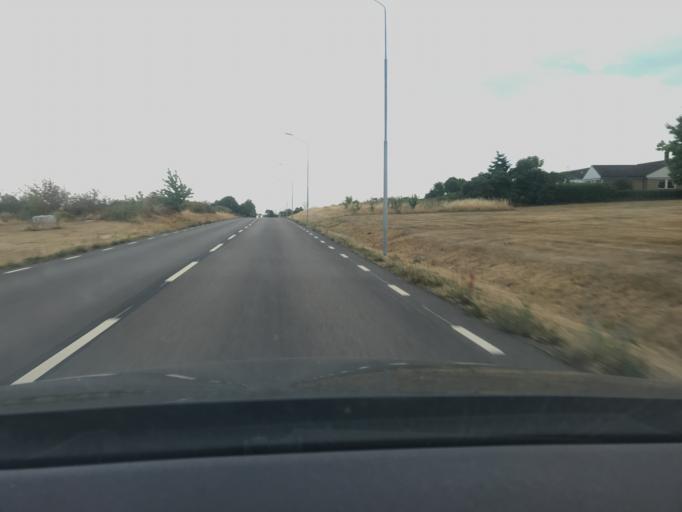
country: SE
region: Skane
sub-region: Simrishamns Kommun
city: Simrishamn
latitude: 55.5440
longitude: 14.3530
